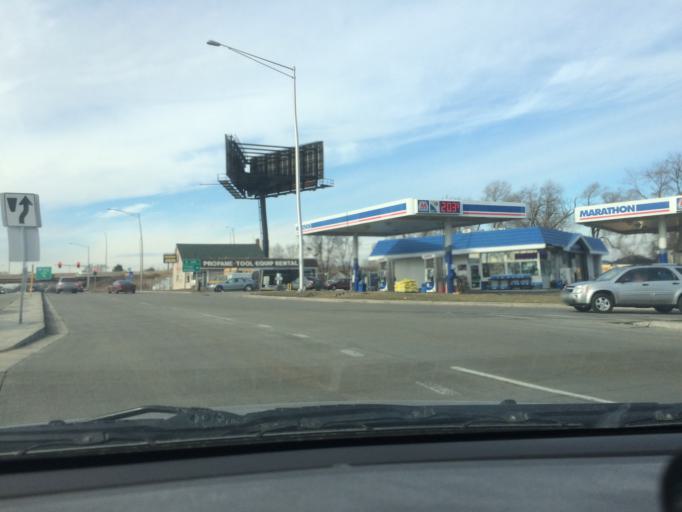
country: US
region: Illinois
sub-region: DuPage County
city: Itasca
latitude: 41.9505
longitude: -88.0320
